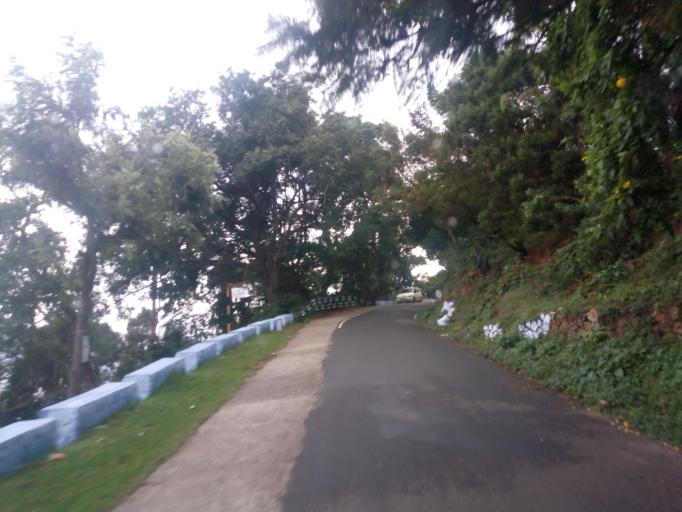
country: IN
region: Tamil Nadu
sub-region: Nilgiri
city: Kotagiri
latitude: 11.3621
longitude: 76.8474
